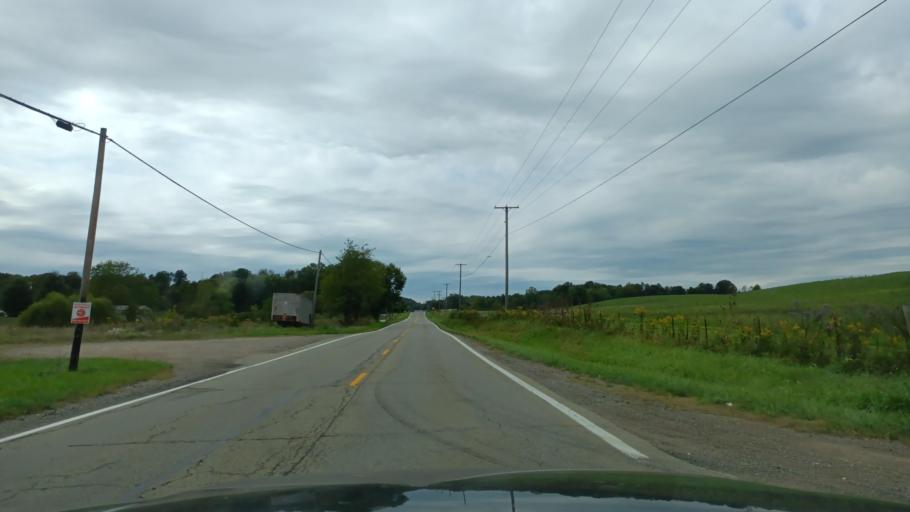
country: US
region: Ohio
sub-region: Vinton County
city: McArthur
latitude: 39.2566
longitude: -82.4989
